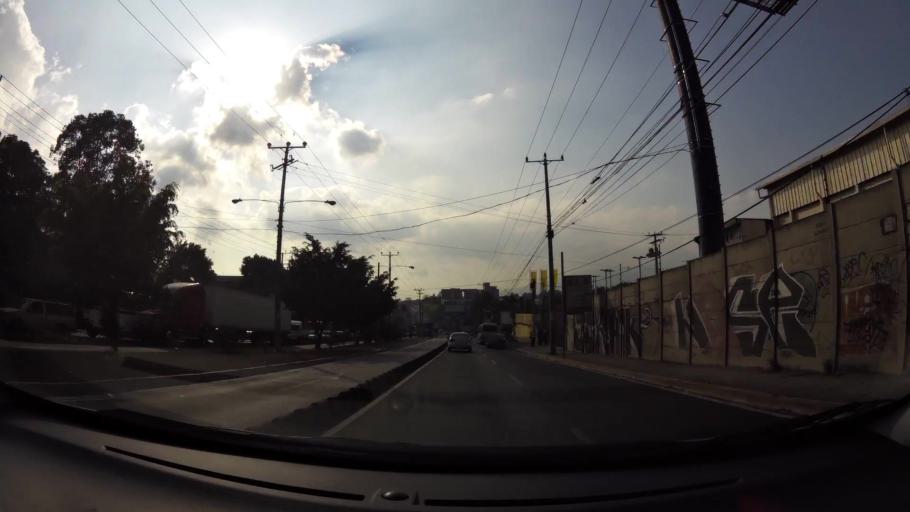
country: SV
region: San Salvador
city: Delgado
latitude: 13.7014
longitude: -89.1624
